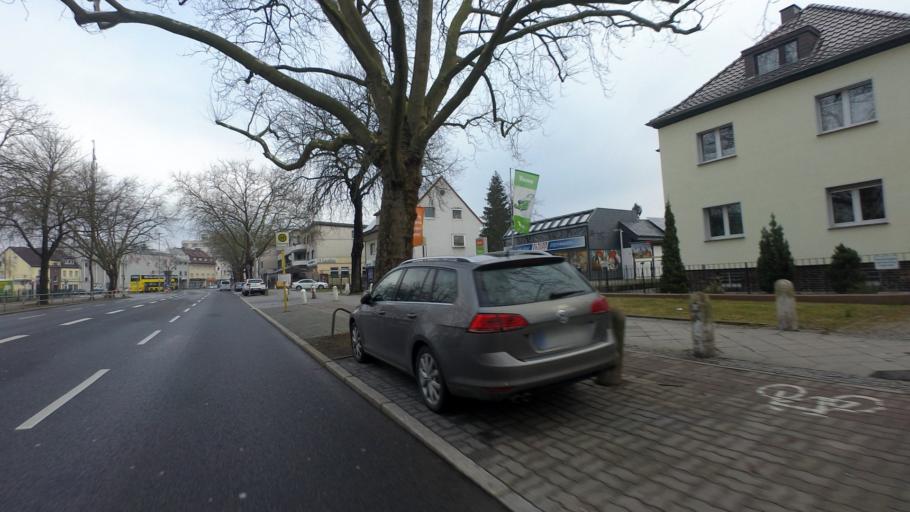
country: DE
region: Berlin
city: Wittenau
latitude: 52.5932
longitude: 13.3346
